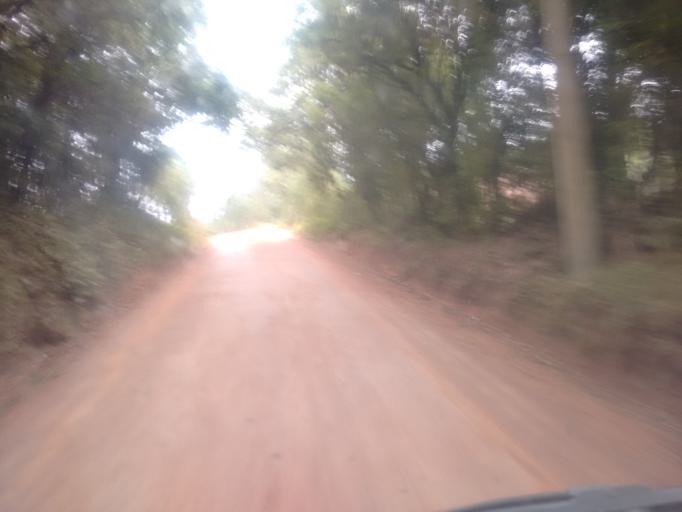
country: BR
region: Rio Grande do Sul
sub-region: Camaqua
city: Camaqua
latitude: -30.7284
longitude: -51.8435
